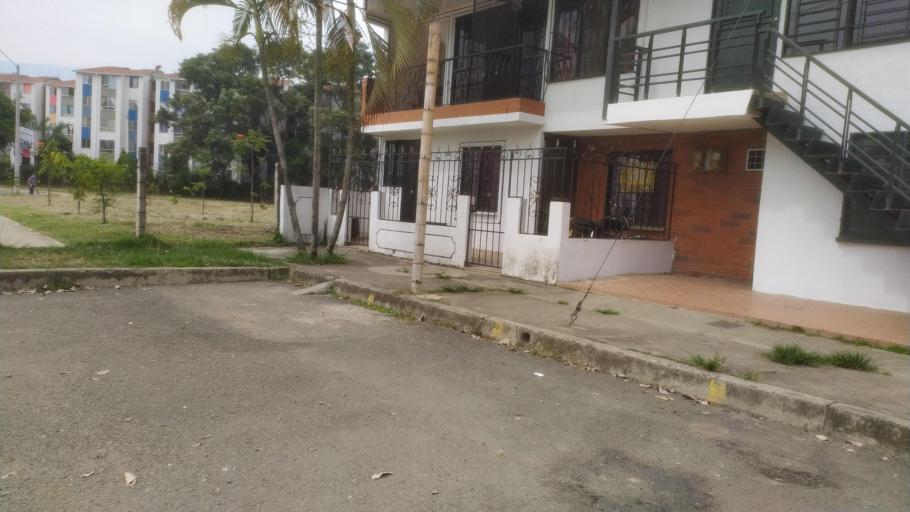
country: CO
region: Valle del Cauca
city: Jamundi
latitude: 3.2370
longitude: -76.5063
